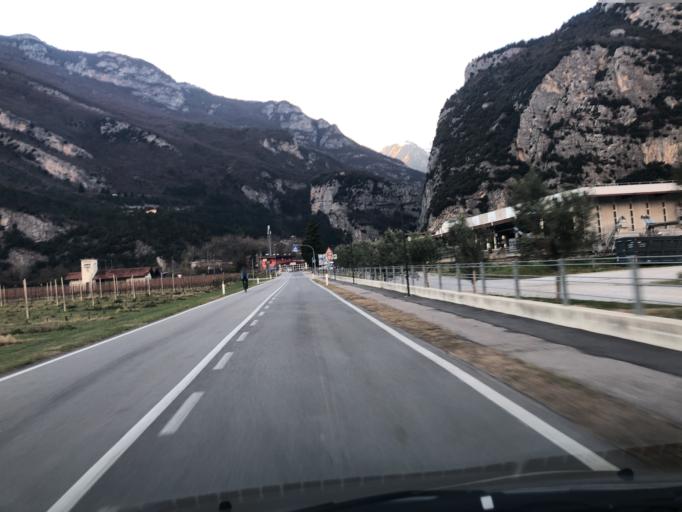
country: IT
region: Trentino-Alto Adige
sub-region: Provincia di Trento
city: Pietramurata
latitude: 46.0442
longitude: 10.9547
